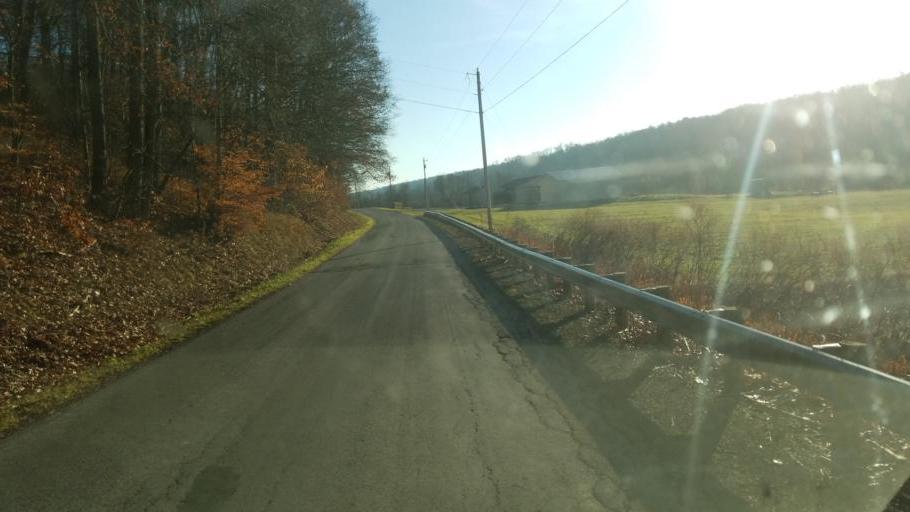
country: US
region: Ohio
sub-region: Wayne County
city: Wooster
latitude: 40.9017
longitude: -82.0075
